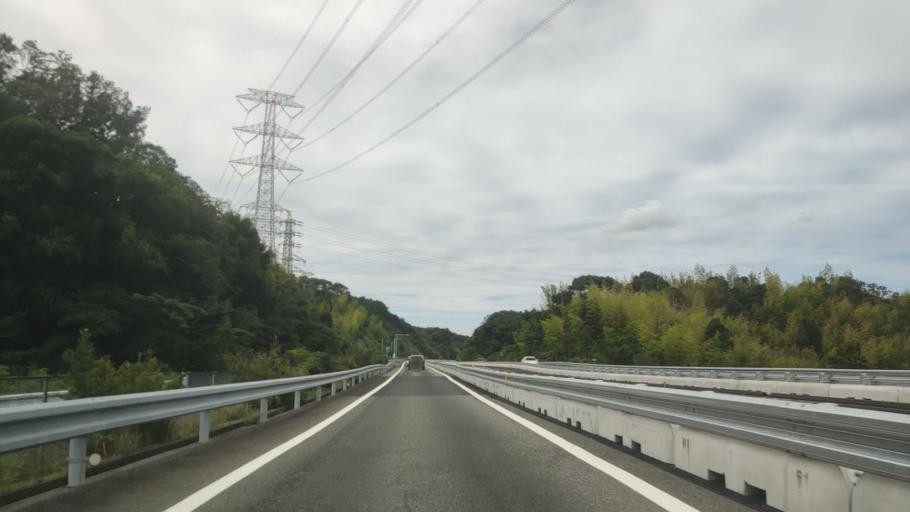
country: JP
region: Wakayama
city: Gobo
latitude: 33.8607
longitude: 135.2013
